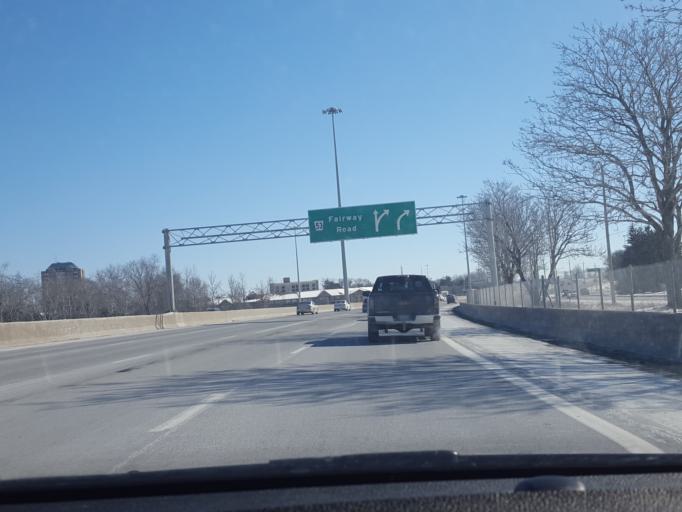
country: CA
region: Ontario
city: Kitchener
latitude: 43.4309
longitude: -80.4411
